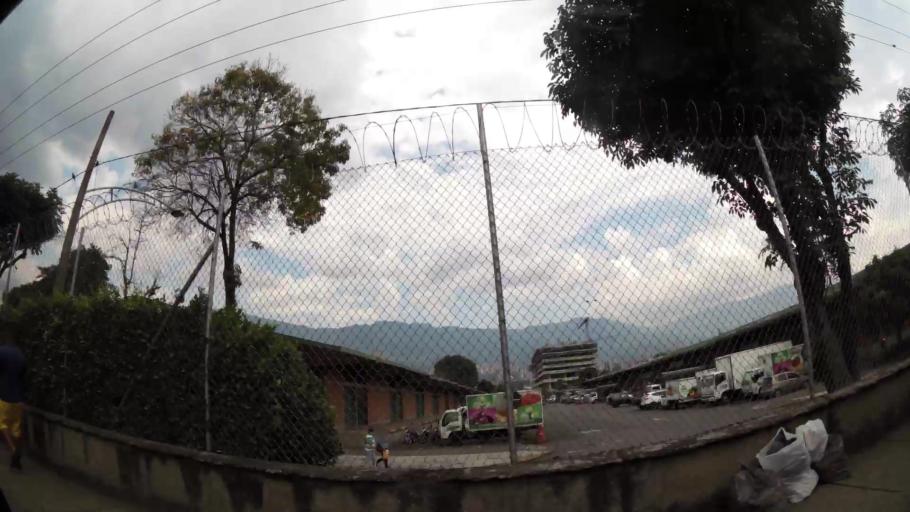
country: CO
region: Antioquia
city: Itagui
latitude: 6.1882
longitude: -75.5926
